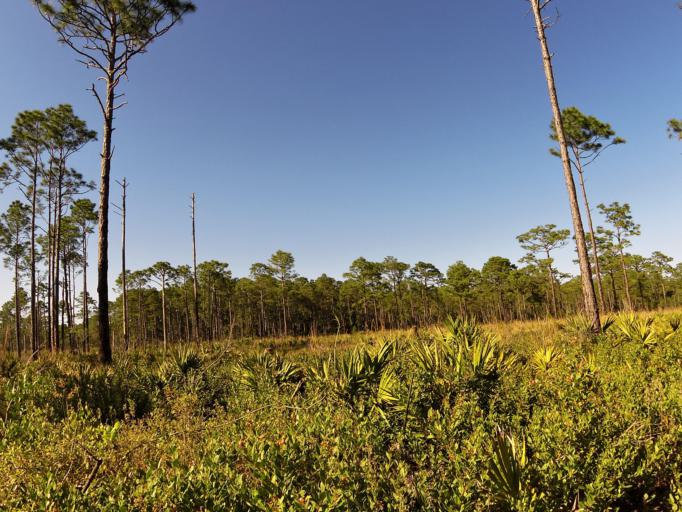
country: US
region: Florida
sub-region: Duval County
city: Atlantic Beach
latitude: 30.4749
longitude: -81.4975
